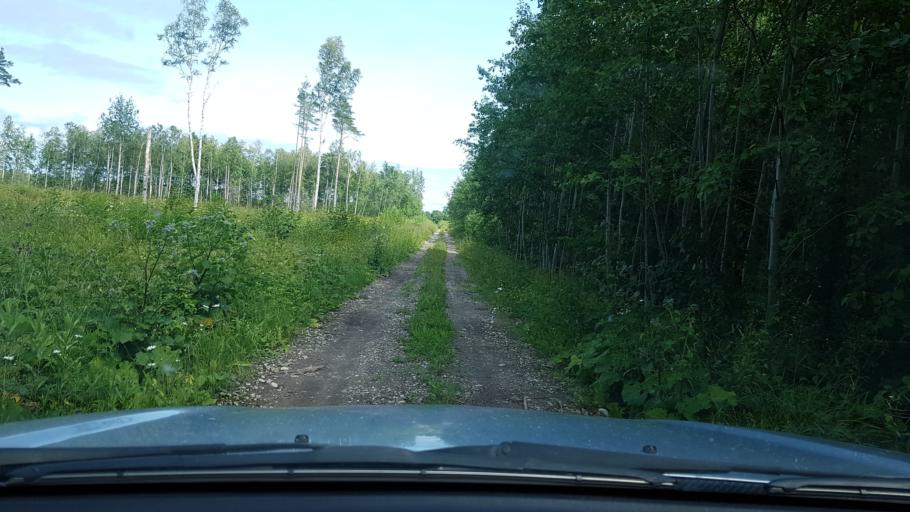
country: EE
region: Ida-Virumaa
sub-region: Sillamaee linn
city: Sillamae
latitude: 59.3583
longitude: 27.7818
